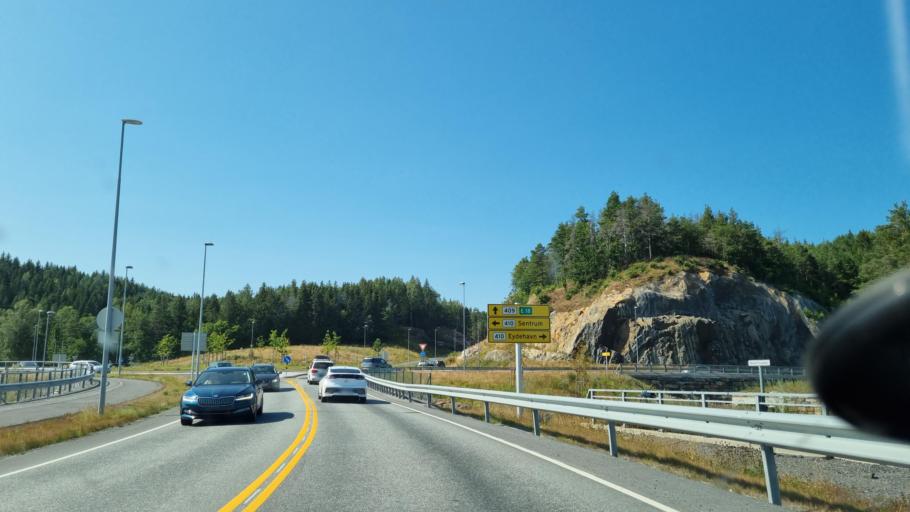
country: NO
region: Aust-Agder
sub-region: Arendal
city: Arendal
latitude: 58.4767
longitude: 8.8189
